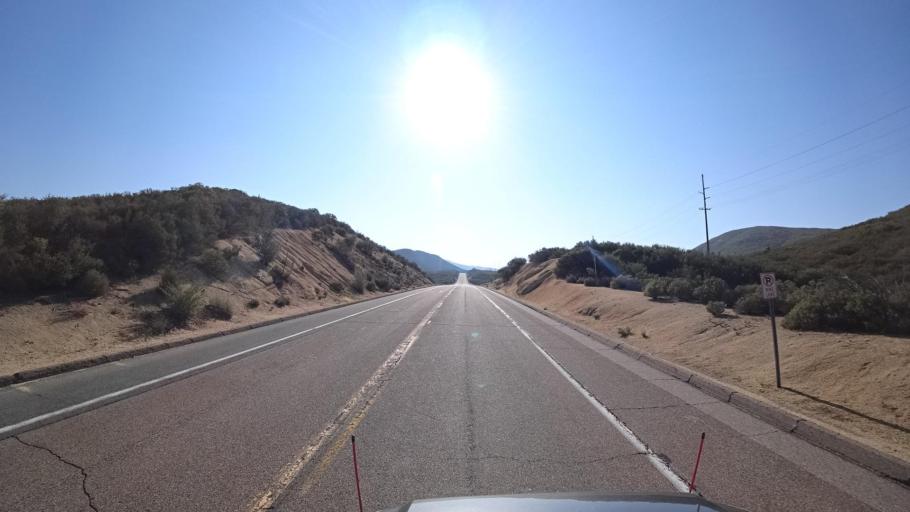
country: US
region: California
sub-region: San Diego County
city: Pine Valley
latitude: 32.8173
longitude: -116.5191
